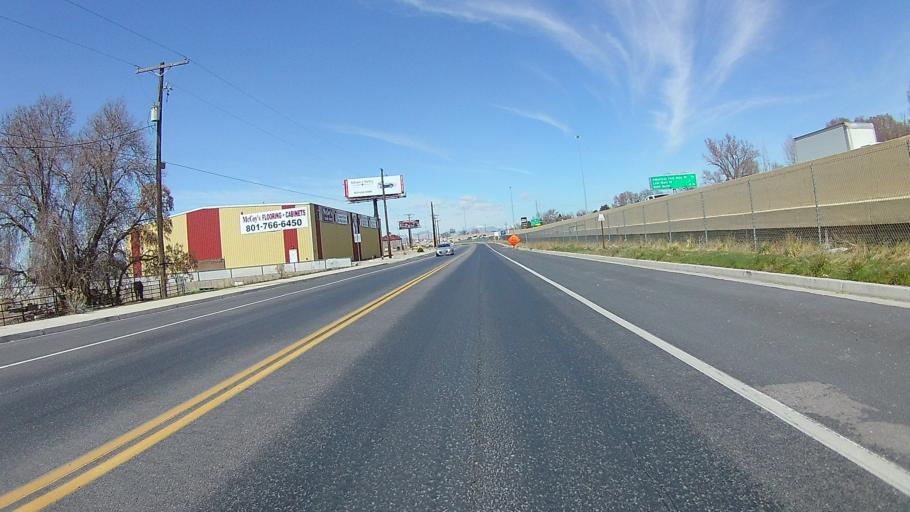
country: US
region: Utah
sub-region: Utah County
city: American Fork
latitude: 40.3693
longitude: -111.7997
